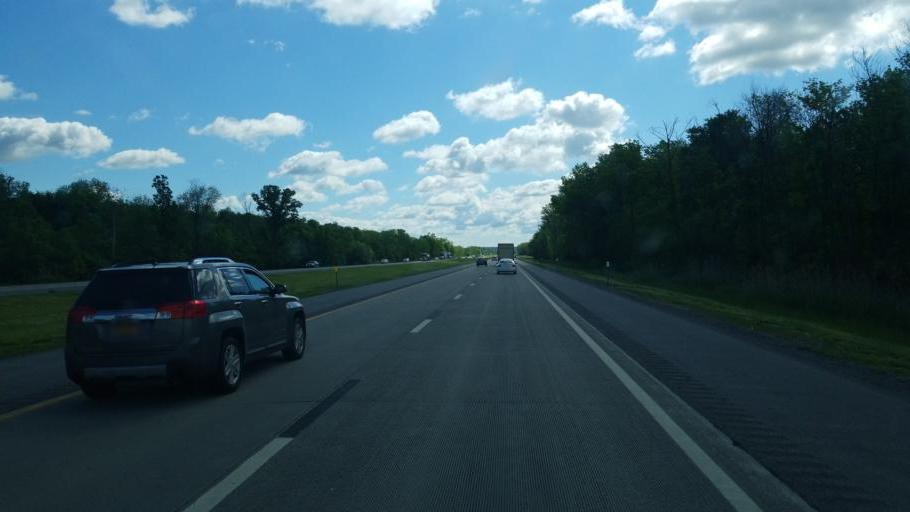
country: US
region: New York
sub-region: Onondaga County
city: Peru
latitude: 43.0830
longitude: -76.4375
